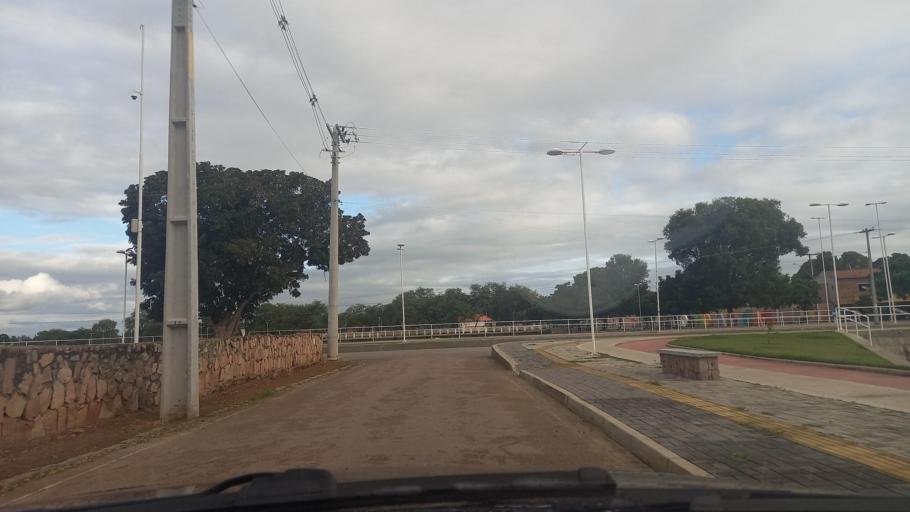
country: BR
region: Bahia
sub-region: Paulo Afonso
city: Paulo Afonso
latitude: -9.3963
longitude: -38.2133
